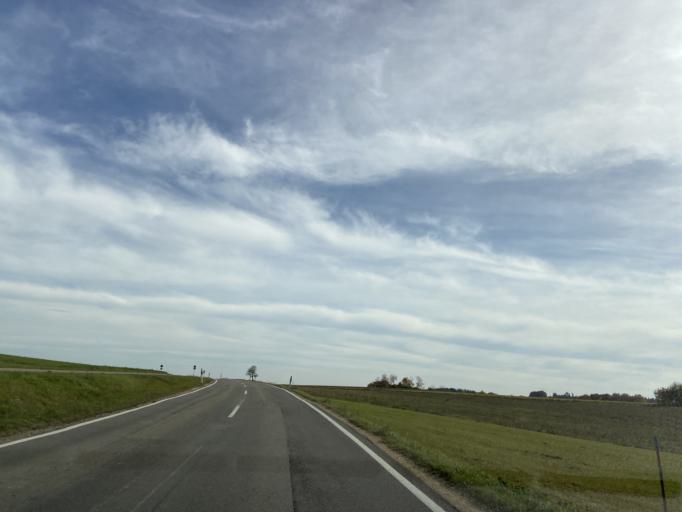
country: DE
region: Baden-Wuerttemberg
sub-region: Tuebingen Region
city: Stetten am Kalten Markt
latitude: 48.1187
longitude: 9.0398
